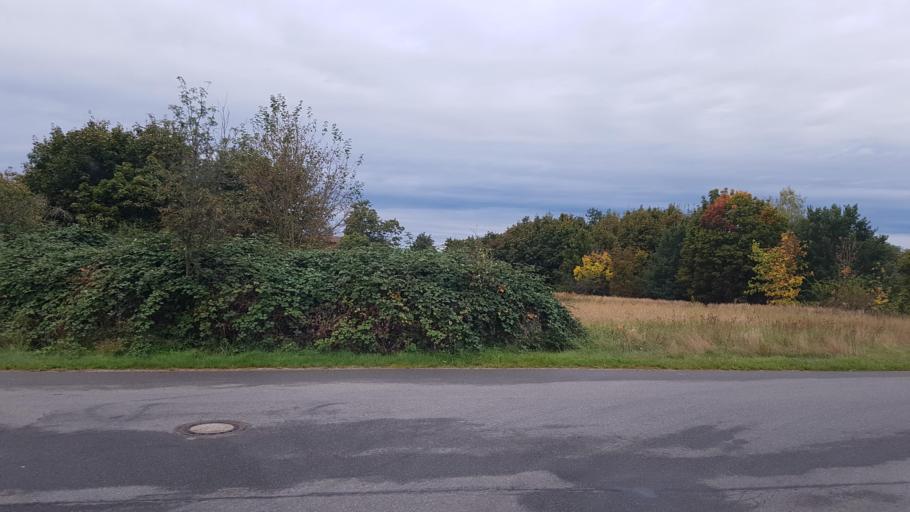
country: DE
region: Brandenburg
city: Golssen
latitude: 51.9742
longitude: 13.5769
